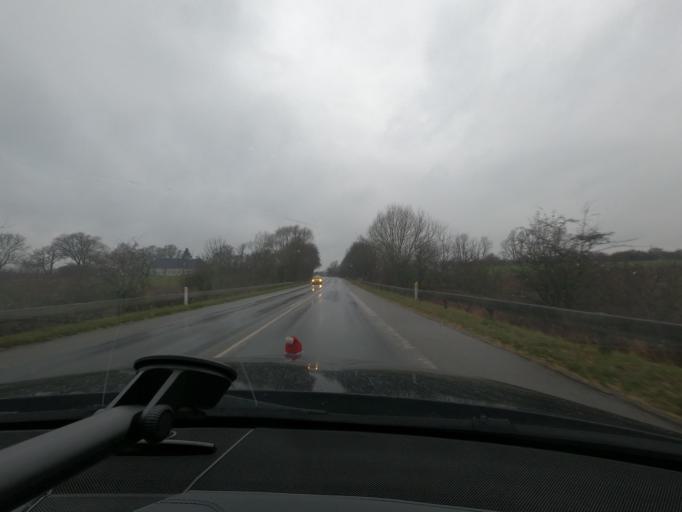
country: DK
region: South Denmark
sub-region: Sonderborg Kommune
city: Horuphav
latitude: 54.8980
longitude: 9.9607
